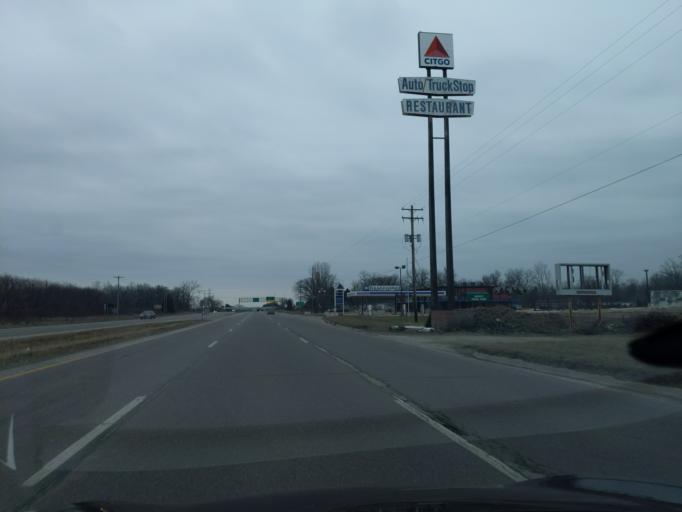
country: US
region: Michigan
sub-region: Eaton County
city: Dimondale
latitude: 42.6714
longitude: -84.6599
